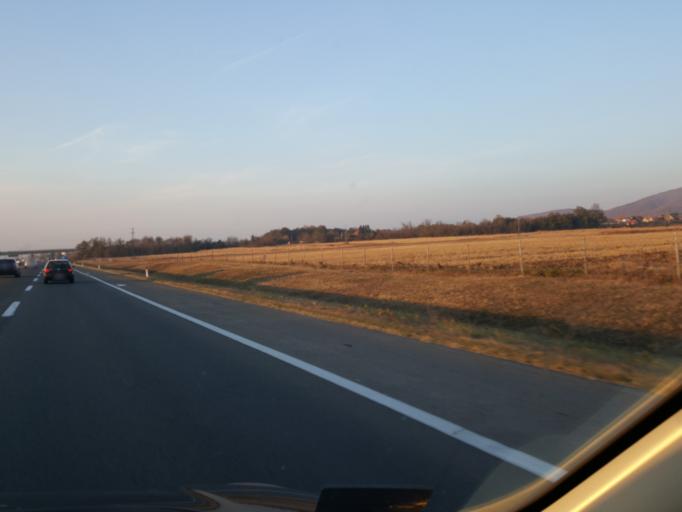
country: RS
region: Central Serbia
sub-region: Nisavski Okrug
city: Nis
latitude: 43.3721
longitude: 21.8163
